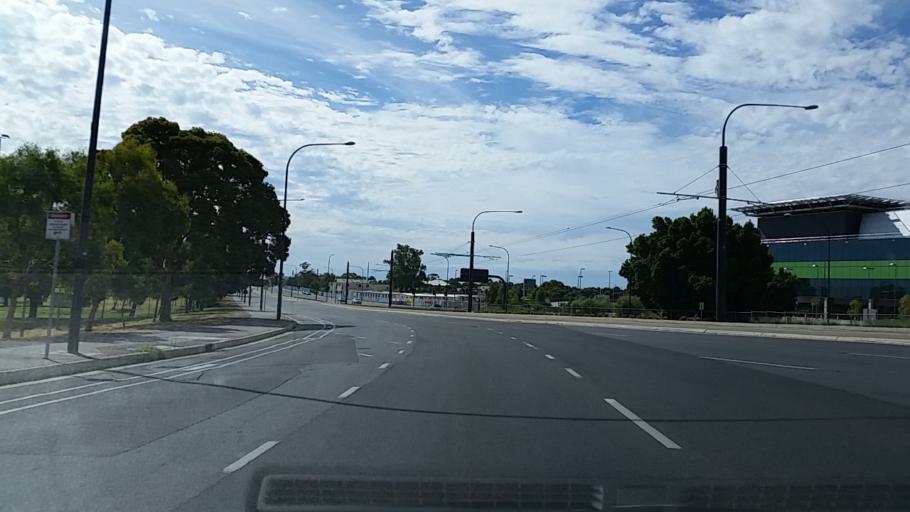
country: AU
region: South Australia
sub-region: Adelaide
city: Adelaide
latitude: -34.9222
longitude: 138.5867
